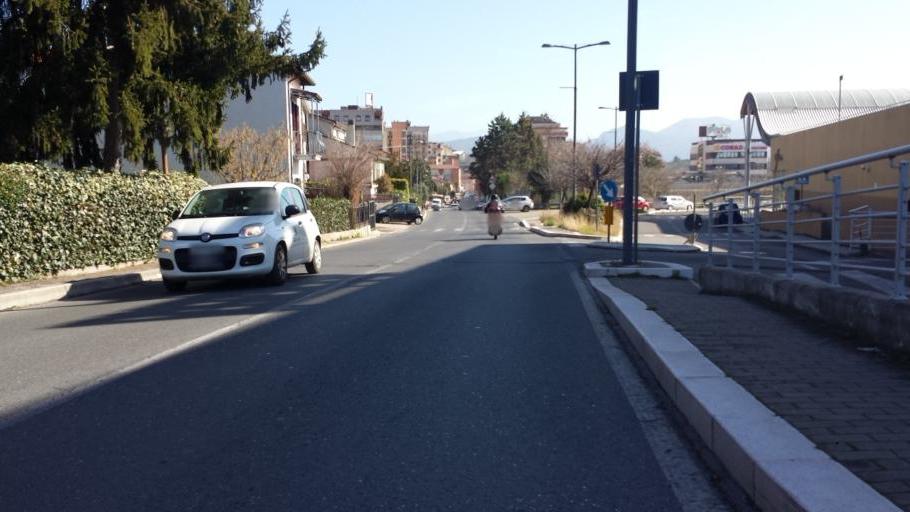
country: IT
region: Umbria
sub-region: Provincia di Terni
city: Terni
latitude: 42.5817
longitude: 12.6188
